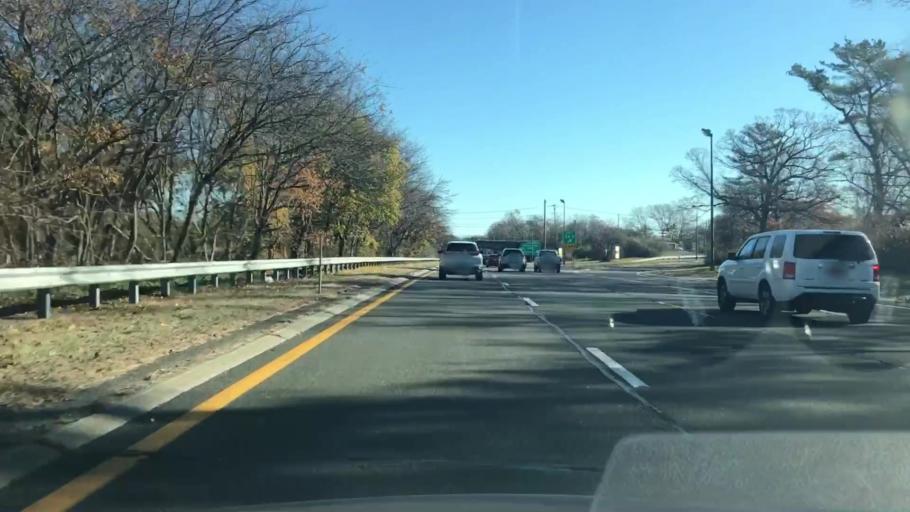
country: US
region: New York
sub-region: Nassau County
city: North Merrick
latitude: 40.6898
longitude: -73.5658
